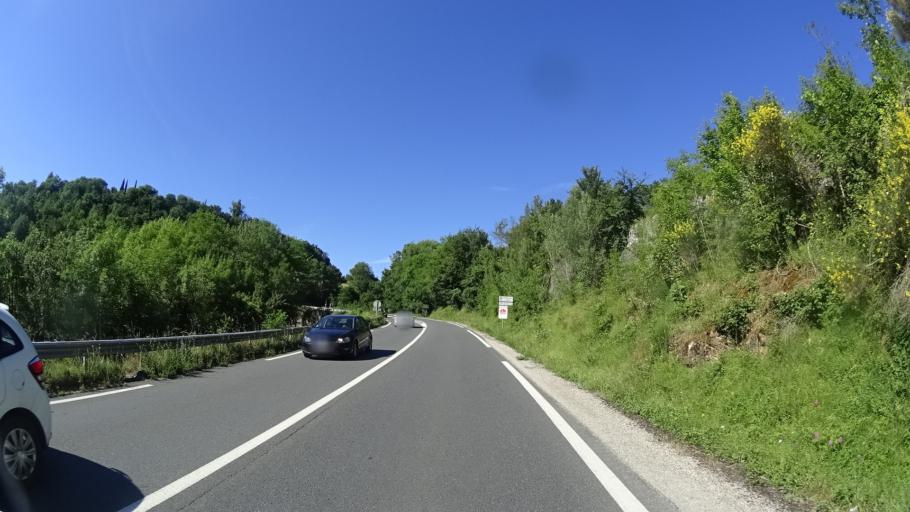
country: FR
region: Midi-Pyrenees
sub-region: Departement de l'Aveyron
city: Capdenac-Gare
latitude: 44.5838
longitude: 2.0687
